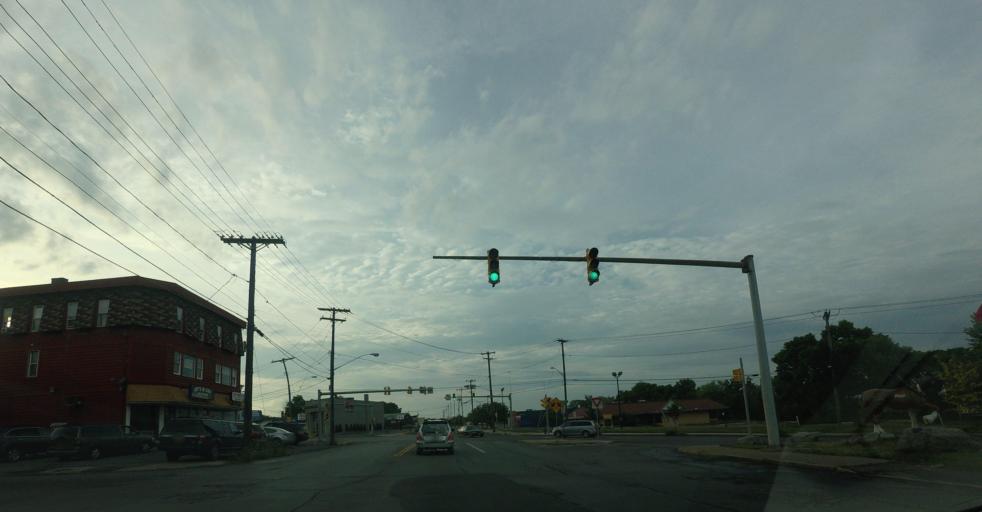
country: US
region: New York
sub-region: Onondaga County
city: Solvay
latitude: 43.0517
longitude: -76.1832
